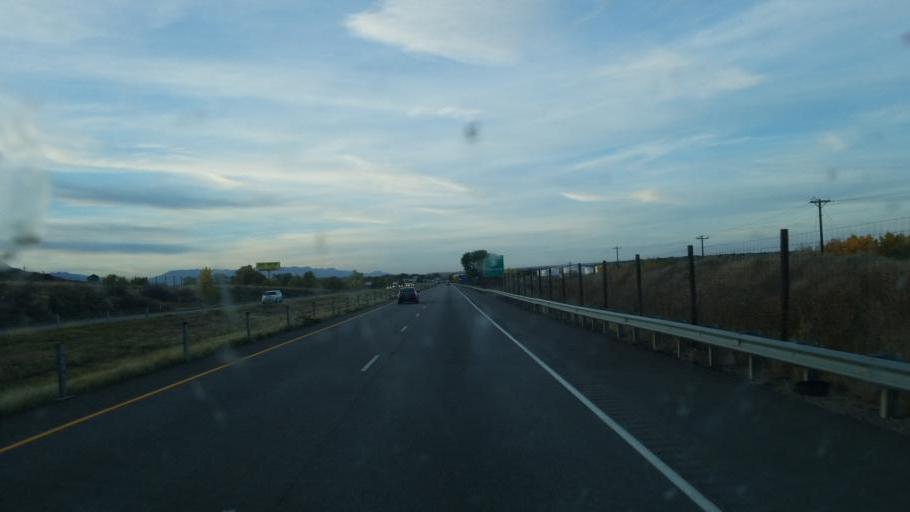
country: US
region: Colorado
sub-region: El Paso County
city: Fountain
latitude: 38.6567
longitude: -104.6988
